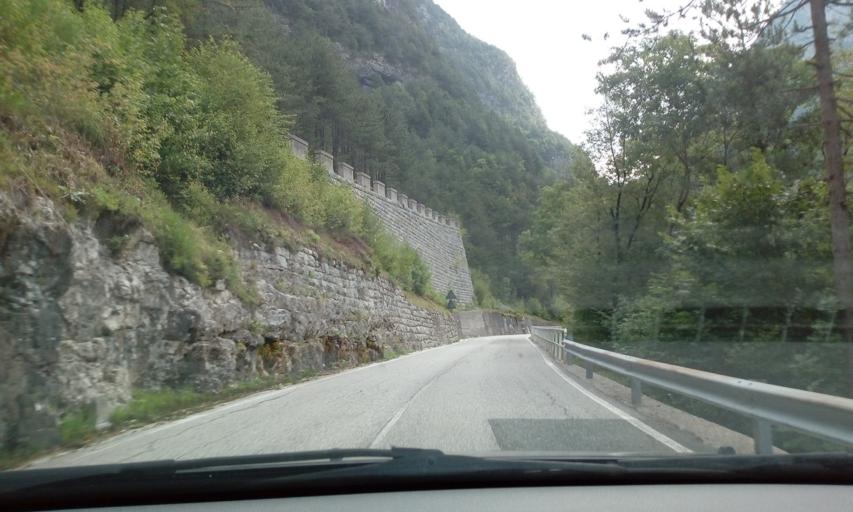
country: IT
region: Friuli Venezia Giulia
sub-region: Provincia di Udine
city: Chiusaforte
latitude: 46.3967
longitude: 13.3338
